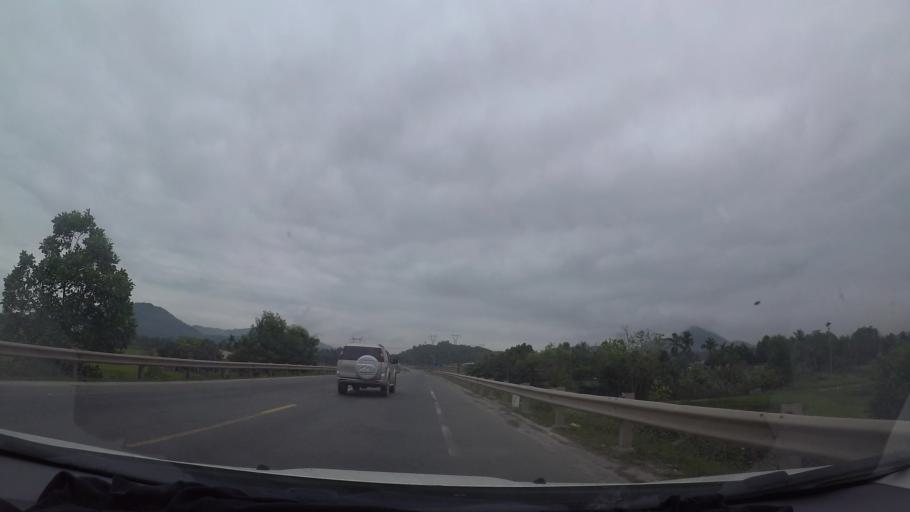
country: VN
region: Da Nang
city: Lien Chieu
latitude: 16.0768
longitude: 108.0869
